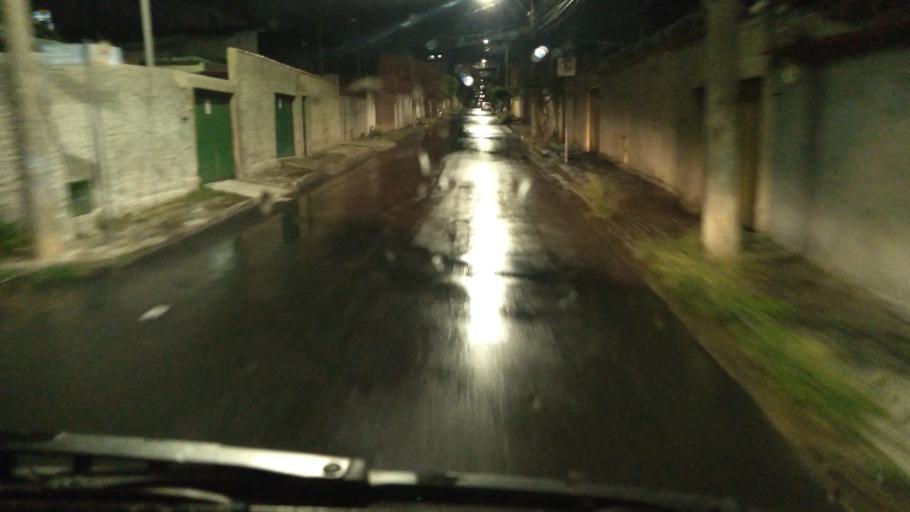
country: BR
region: Minas Gerais
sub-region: Belo Horizonte
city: Belo Horizonte
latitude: -19.8981
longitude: -43.9156
